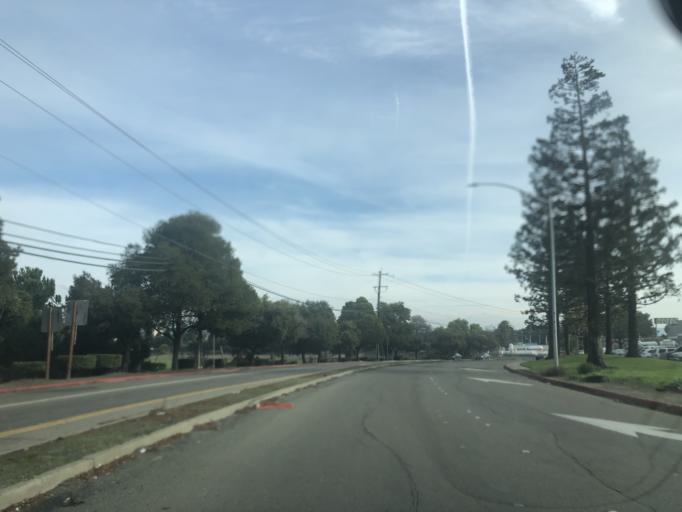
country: US
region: California
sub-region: Contra Costa County
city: Pacheco
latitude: 38.0032
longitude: -122.0507
